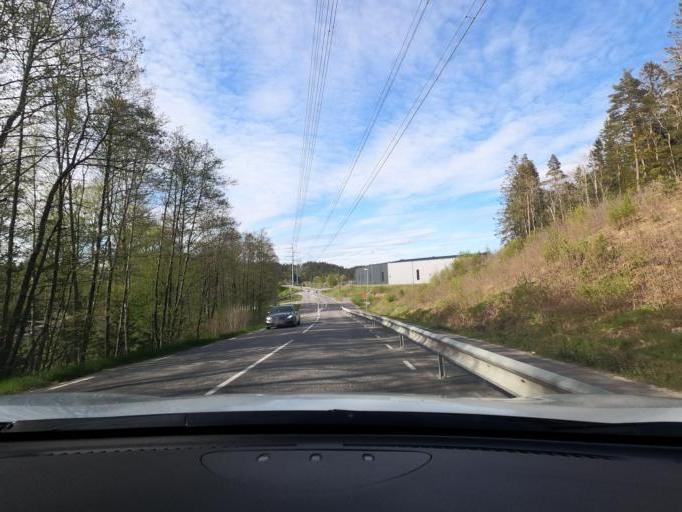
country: SE
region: Vaestra Goetaland
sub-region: Harryda Kommun
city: Landvetter
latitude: 57.6798
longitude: 12.2408
